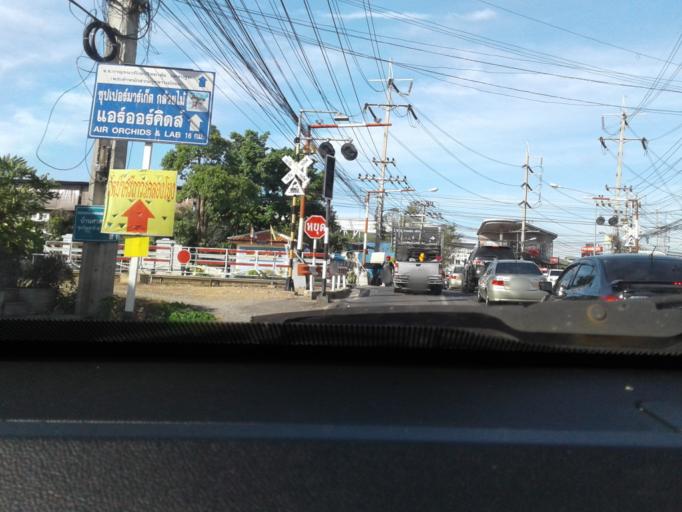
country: TH
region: Nakhon Pathom
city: Salaya
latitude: 13.8024
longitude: 100.3204
